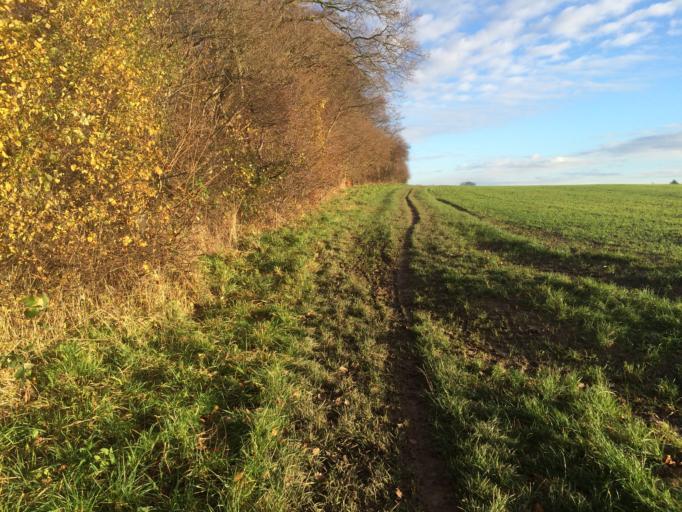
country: DK
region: Capital Region
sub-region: Fureso Kommune
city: Vaerlose
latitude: 55.7898
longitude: 12.3480
